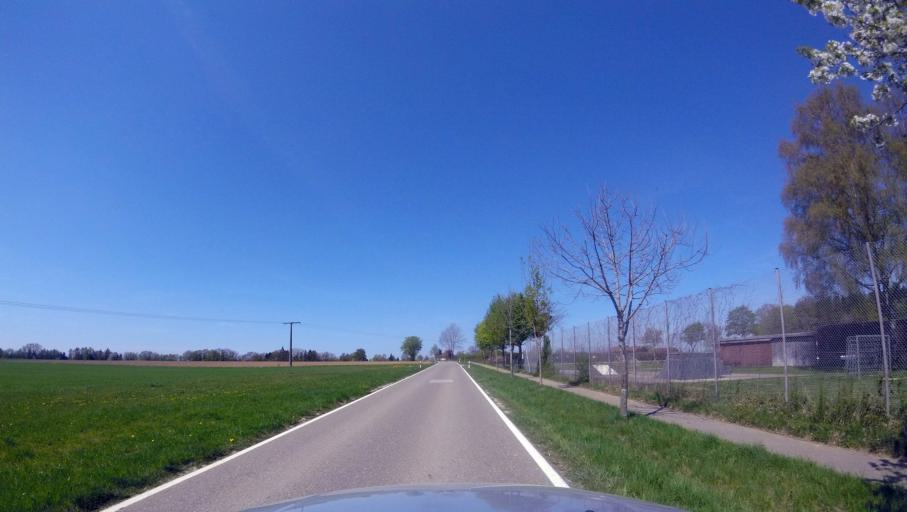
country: DE
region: Baden-Wuerttemberg
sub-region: Regierungsbezirk Stuttgart
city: Durlangen
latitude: 48.8585
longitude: 9.7871
